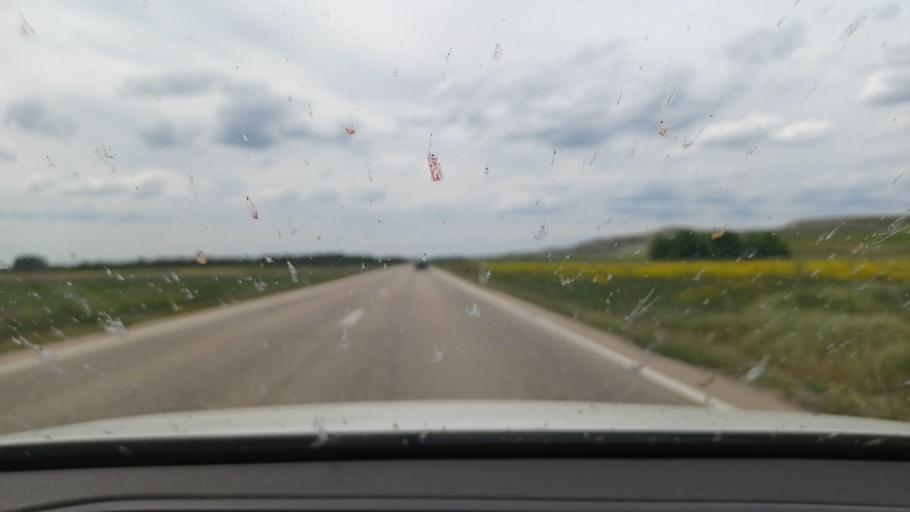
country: ES
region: Castille and Leon
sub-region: Provincia de Segovia
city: Frumales
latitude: 41.3819
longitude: -4.2077
